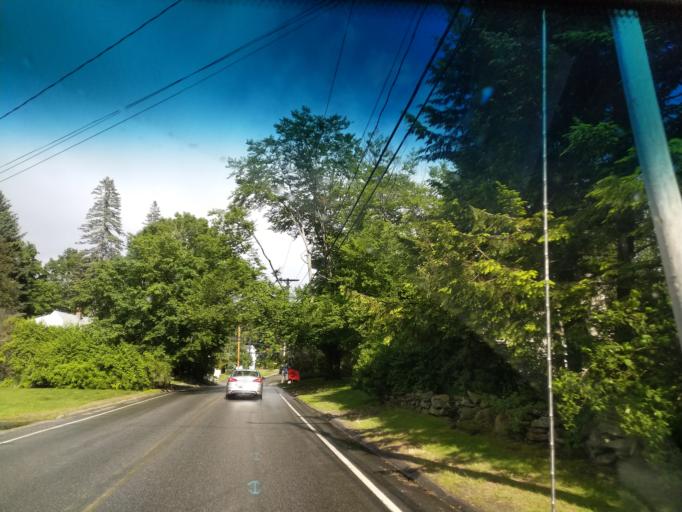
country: US
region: Maine
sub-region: Cumberland County
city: Falmouth
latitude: 43.7468
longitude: -70.2999
